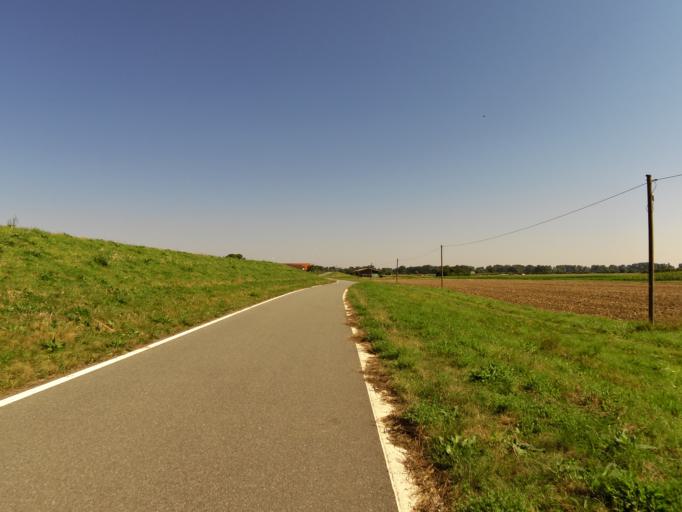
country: DE
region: Rheinland-Pfalz
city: Nackenheim
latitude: 49.9146
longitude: 8.3661
